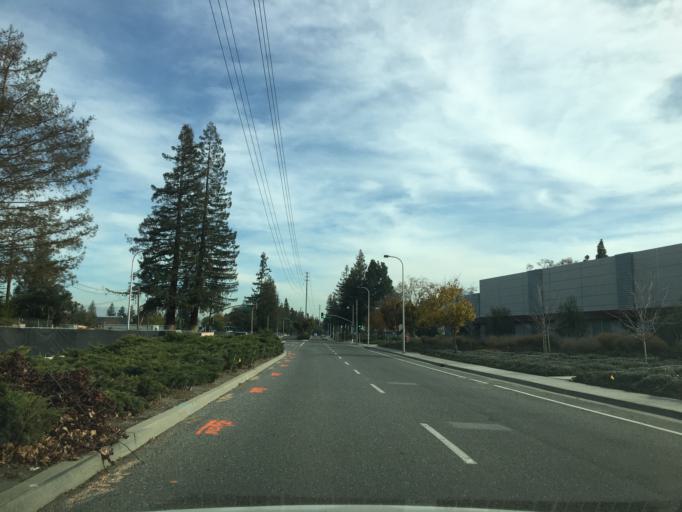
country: US
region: California
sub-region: Santa Clara County
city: Santa Clara
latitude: 37.3798
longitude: -121.9726
